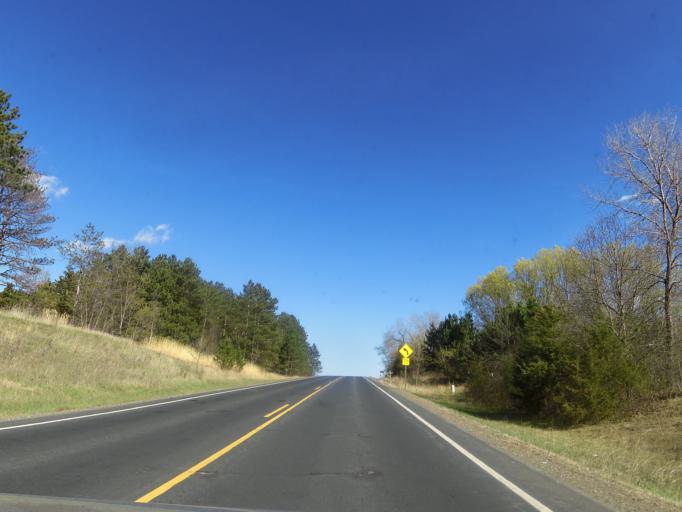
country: US
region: Minnesota
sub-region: Washington County
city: Bayport
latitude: 45.0582
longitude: -92.7485
